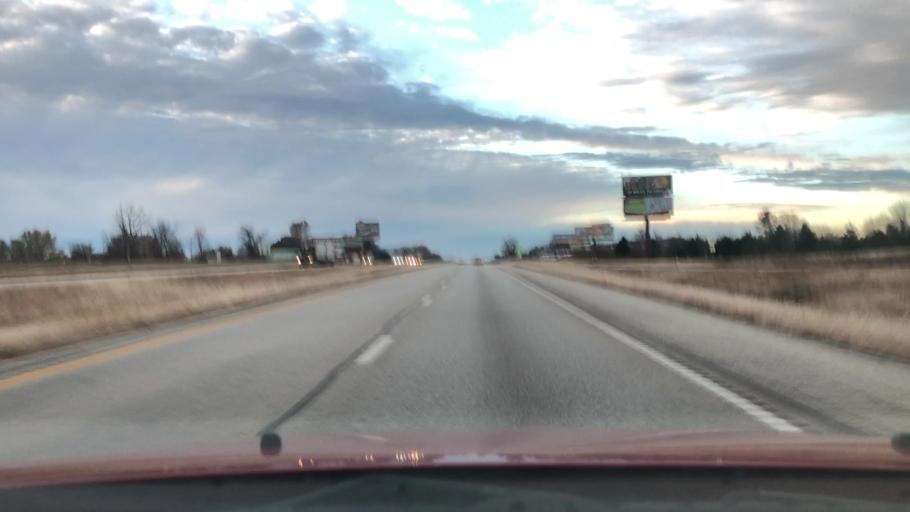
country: US
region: Missouri
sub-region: Christian County
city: Ozark
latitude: 36.9419
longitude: -93.2322
